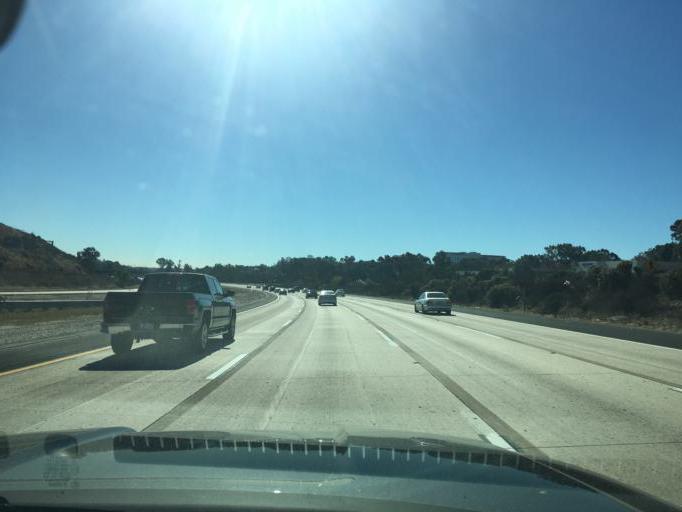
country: US
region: California
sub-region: San Diego County
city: La Mesa
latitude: 32.8409
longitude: -117.1211
